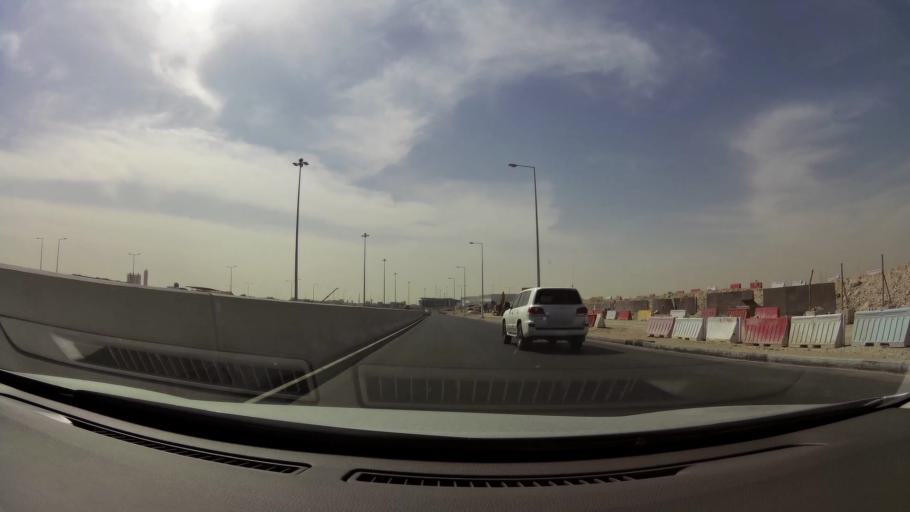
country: QA
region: Baladiyat ar Rayyan
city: Ar Rayyan
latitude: 25.3011
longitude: 51.4273
